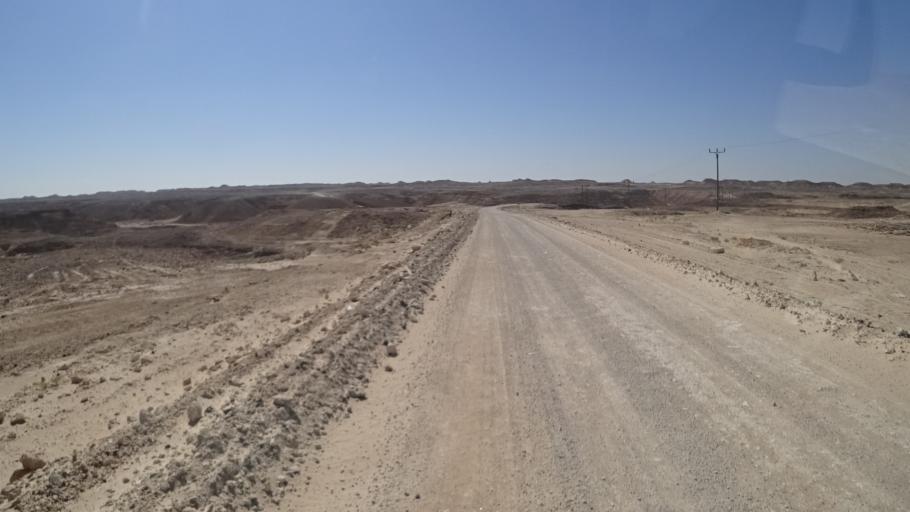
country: YE
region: Al Mahrah
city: Hawf
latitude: 17.3743
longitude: 53.1985
